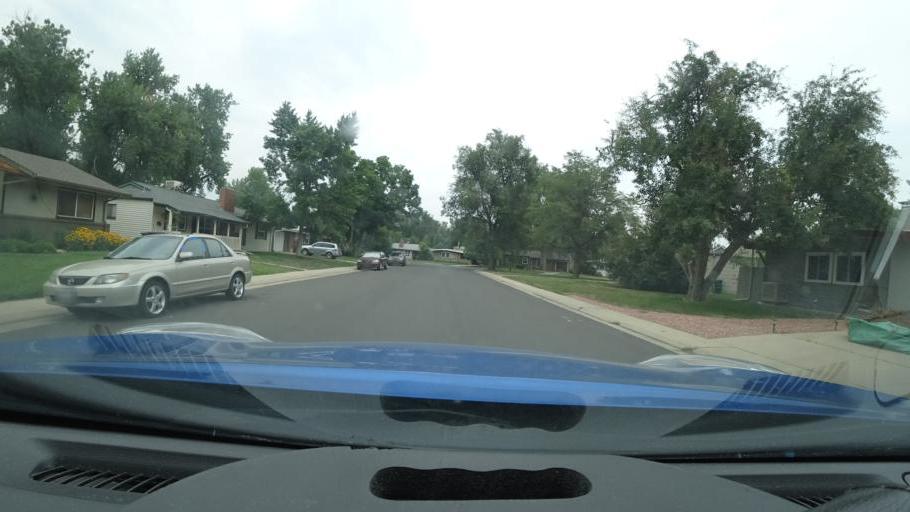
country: US
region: Colorado
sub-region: Arapahoe County
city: Glendale
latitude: 39.6903
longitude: -104.9152
